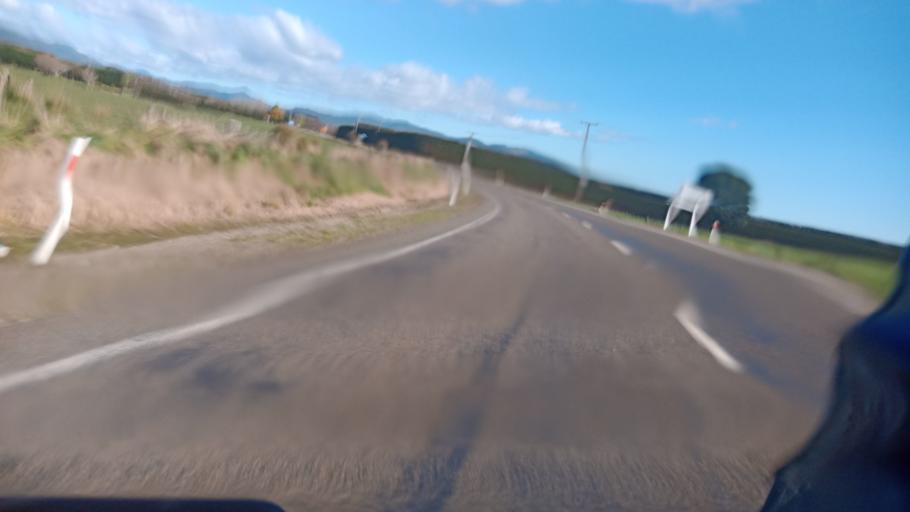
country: NZ
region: Bay of Plenty
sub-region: Opotiki District
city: Opotiki
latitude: -37.9977
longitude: 177.2989
